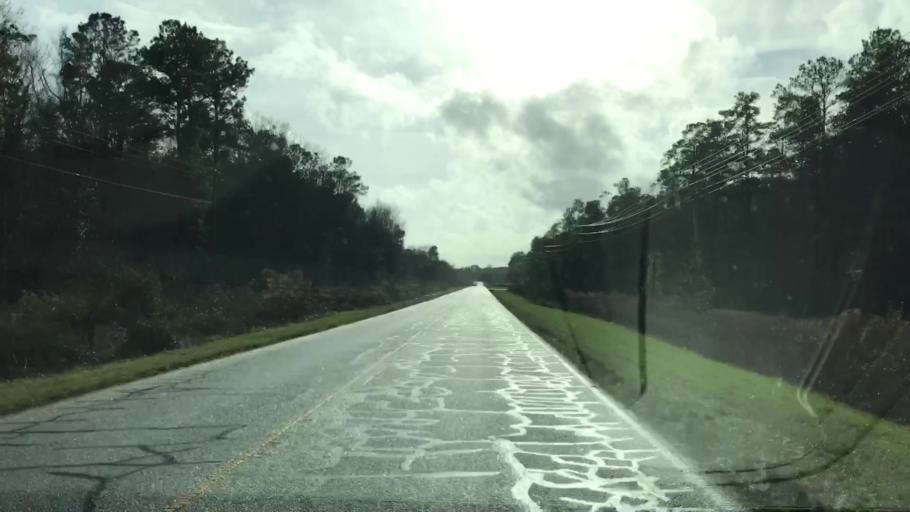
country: US
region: South Carolina
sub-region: Williamsburg County
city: Andrews
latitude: 33.4815
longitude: -79.5542
